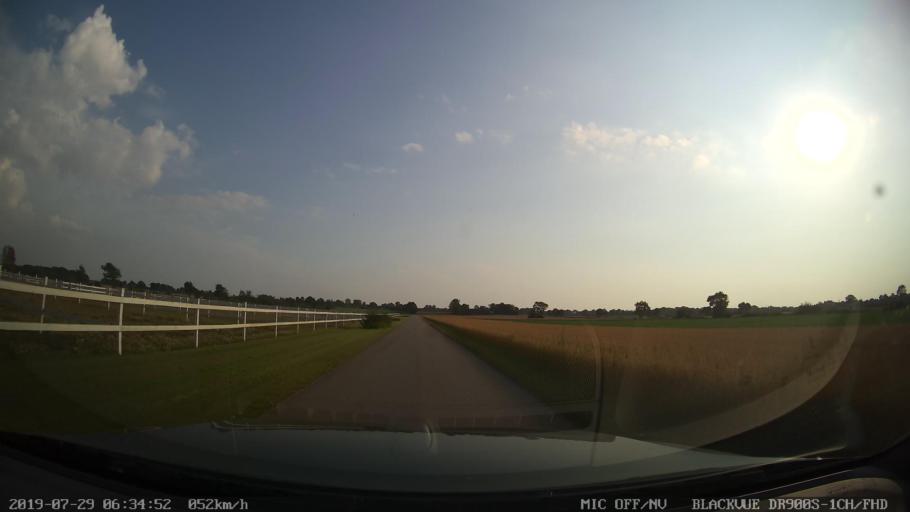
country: SE
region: Skane
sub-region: Helsingborg
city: Odakra
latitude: 56.1171
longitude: 12.7226
